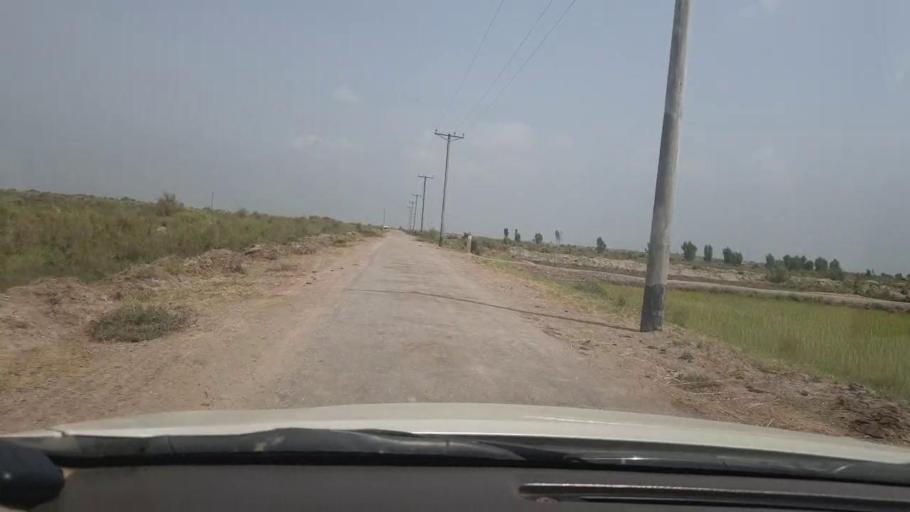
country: PK
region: Sindh
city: Garhi Yasin
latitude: 28.0046
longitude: 68.4999
